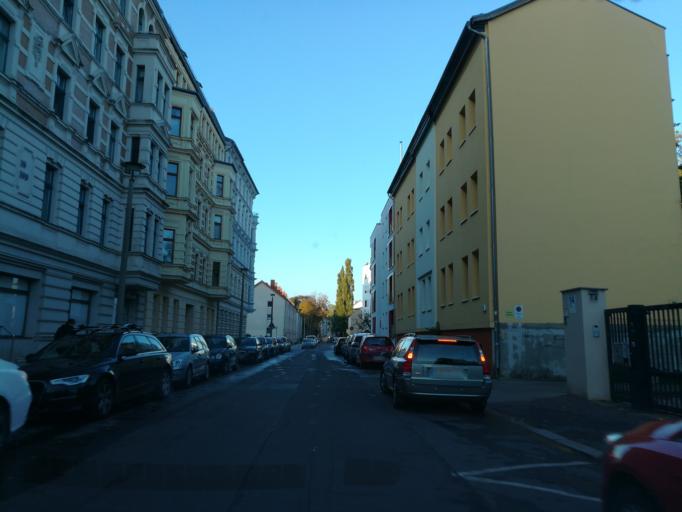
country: DE
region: Saxony-Anhalt
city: Magdeburg
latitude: 52.1308
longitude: 11.6516
